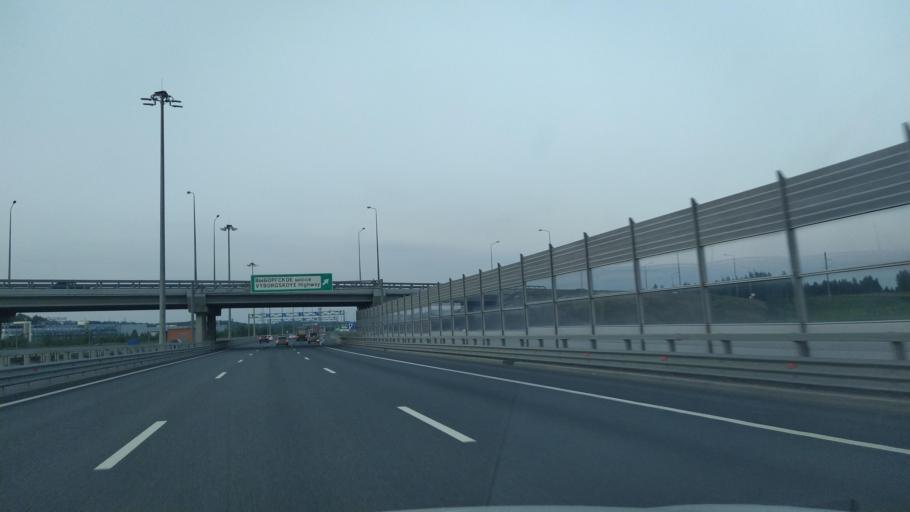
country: RU
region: St.-Petersburg
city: Pargolovo
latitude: 60.0986
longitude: 30.2666
